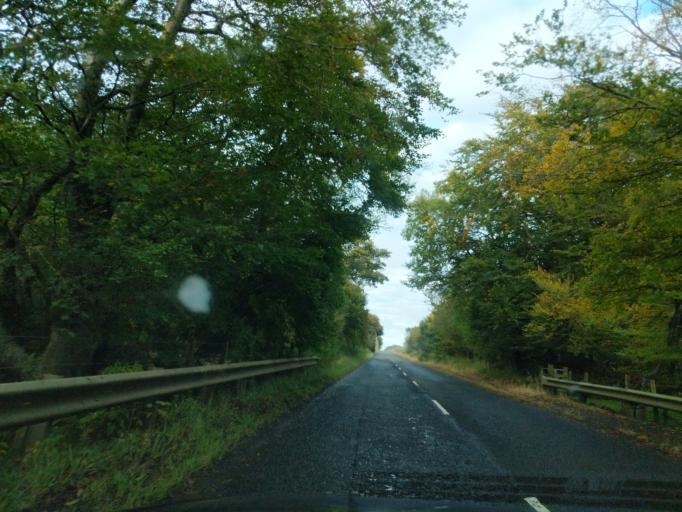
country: GB
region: Scotland
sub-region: Midlothian
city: Penicuik
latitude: 55.8187
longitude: -3.2745
